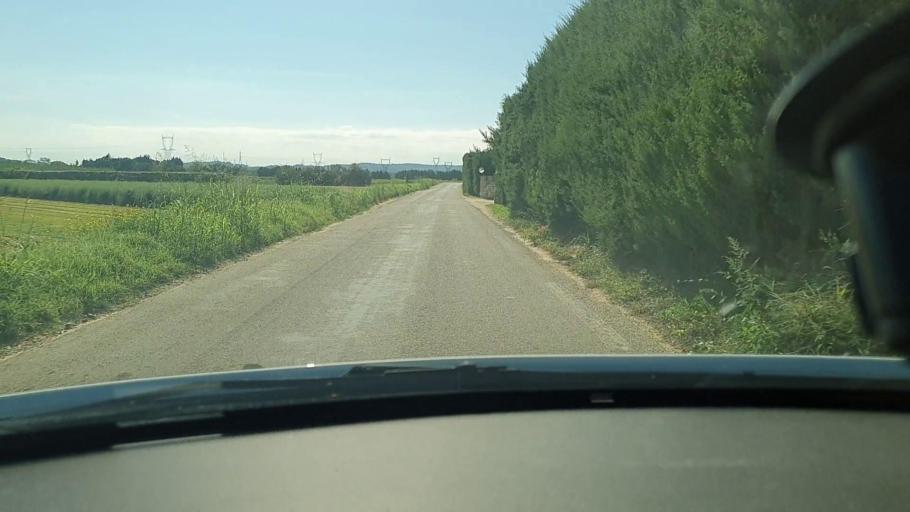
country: FR
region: Languedoc-Roussillon
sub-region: Departement du Gard
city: Saint-Julien-de-Peyrolas
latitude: 44.2879
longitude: 4.5709
